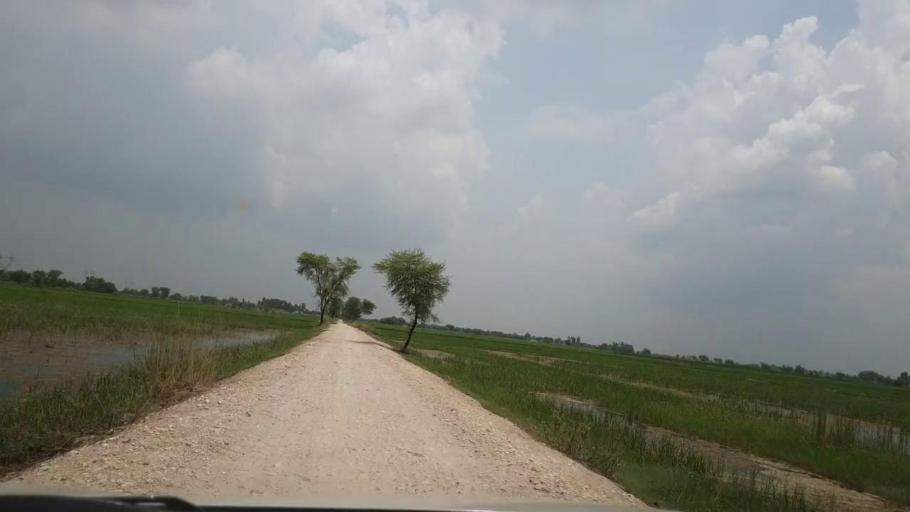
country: PK
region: Sindh
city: Goth Garelo
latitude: 27.4204
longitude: 68.0771
